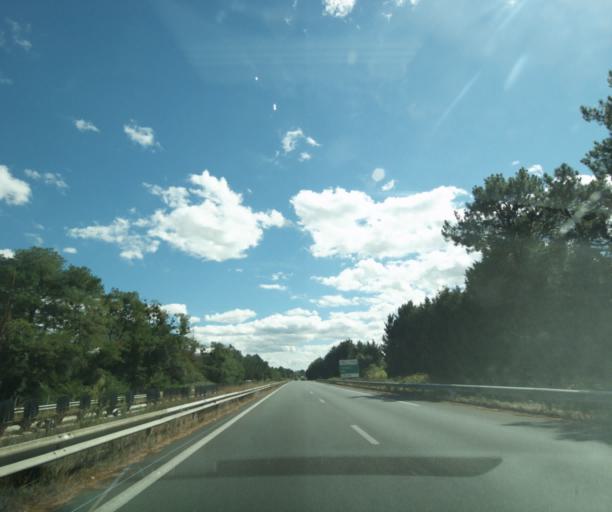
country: FR
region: Aquitaine
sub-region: Departement de la Gironde
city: Toulenne
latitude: 44.5517
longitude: -0.2775
